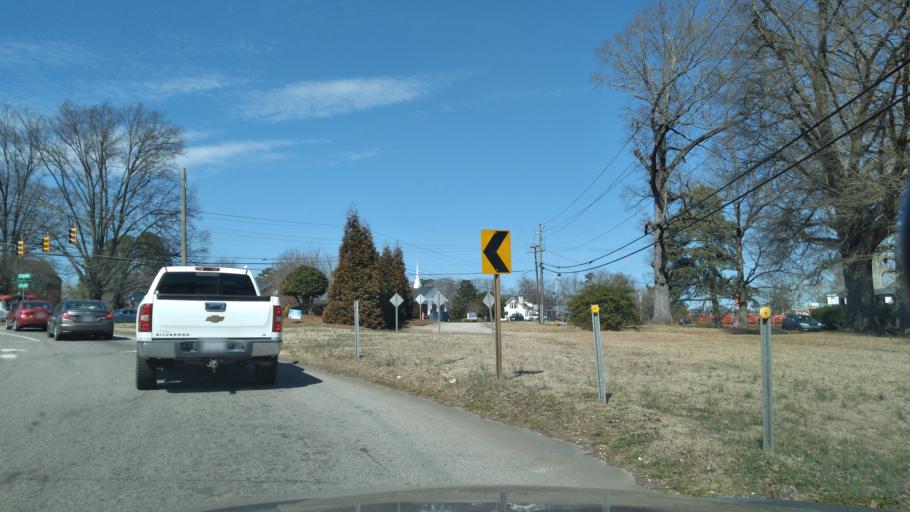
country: US
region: North Carolina
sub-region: Wake County
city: Garner
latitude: 35.7121
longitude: -78.6572
